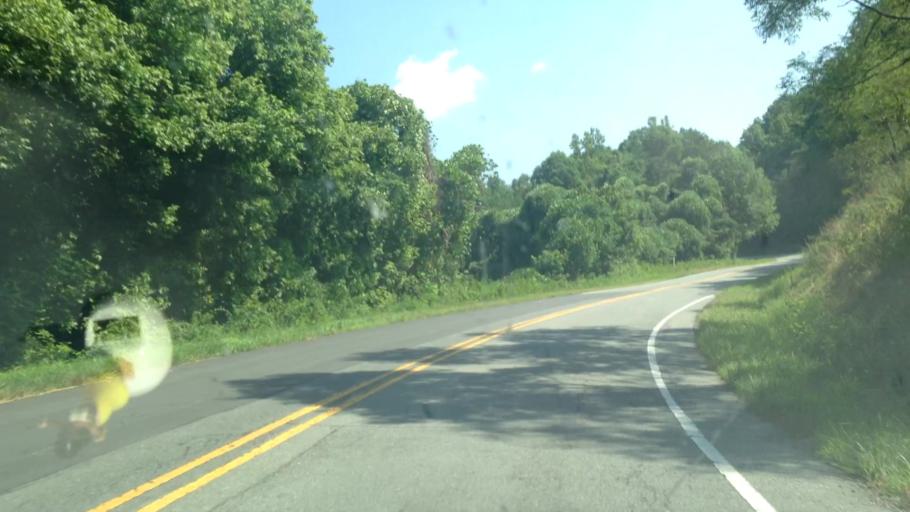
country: US
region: North Carolina
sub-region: Stokes County
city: Walnut Cove
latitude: 36.3175
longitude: -80.0441
